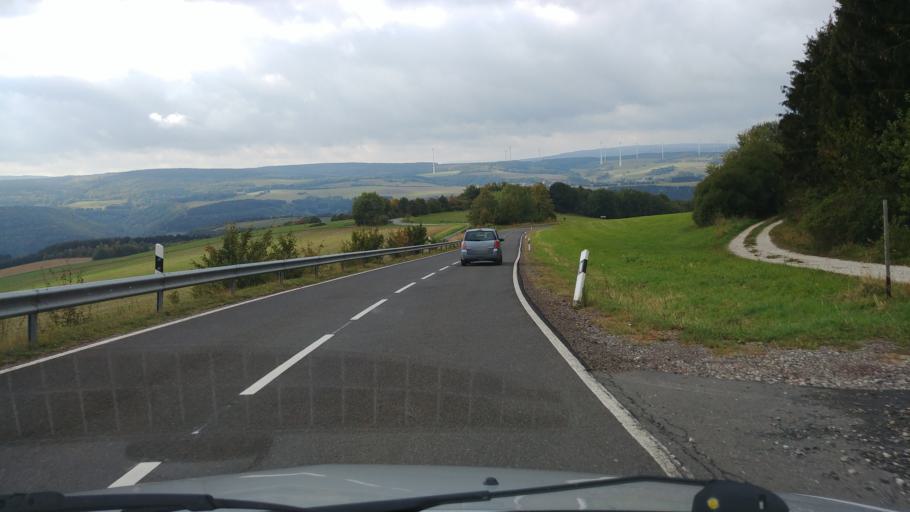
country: DE
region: Rheinland-Pfalz
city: Horath
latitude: 49.8145
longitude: 6.9936
